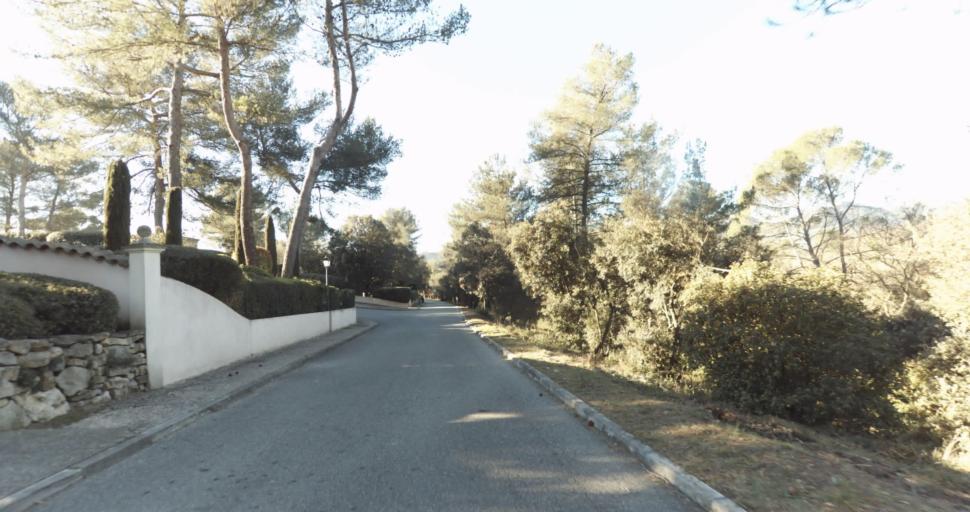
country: FR
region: Provence-Alpes-Cote d'Azur
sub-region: Departement des Bouches-du-Rhone
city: Peypin
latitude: 43.4047
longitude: 5.5724
